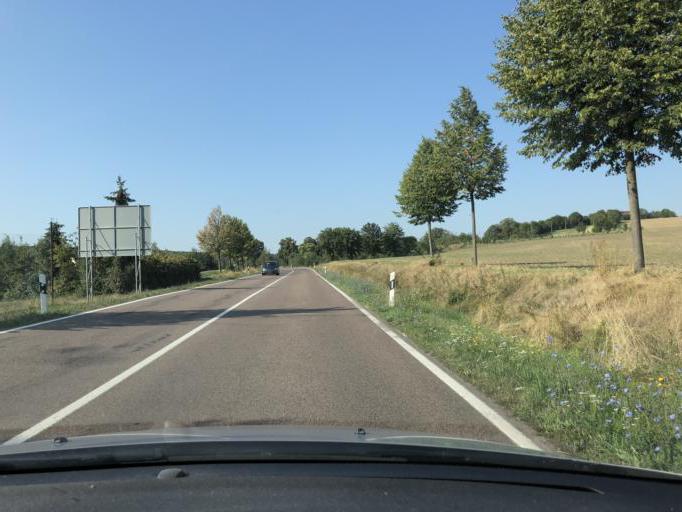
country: DE
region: Saxony-Anhalt
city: Goseck
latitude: 51.2386
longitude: 11.8267
